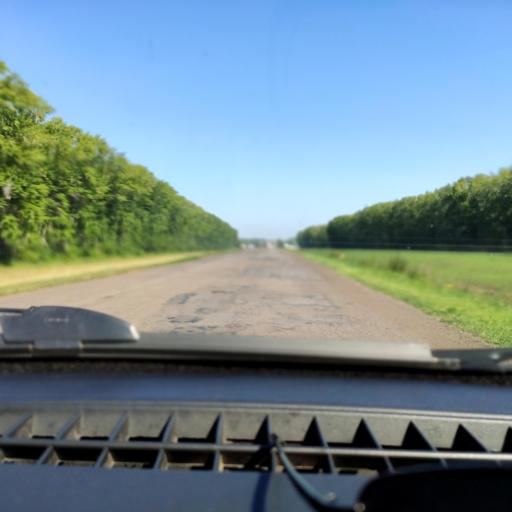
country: RU
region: Bashkortostan
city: Karmaskaly
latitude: 54.3926
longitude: 56.1723
